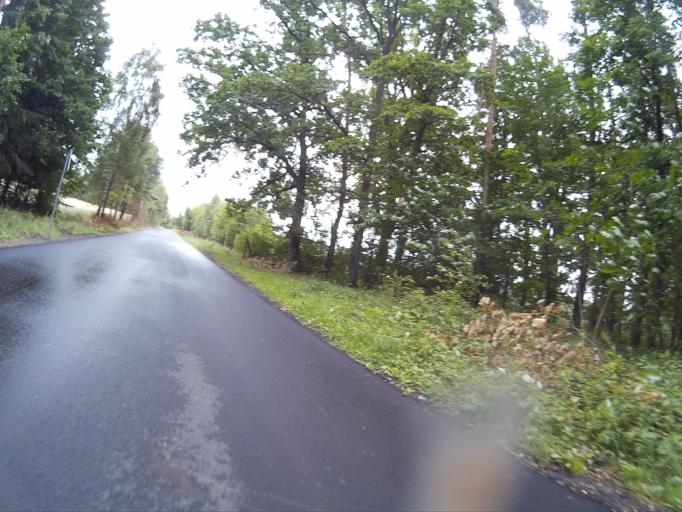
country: PL
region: Kujawsko-Pomorskie
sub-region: Powiat swiecki
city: Lniano
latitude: 53.6037
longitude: 18.1984
